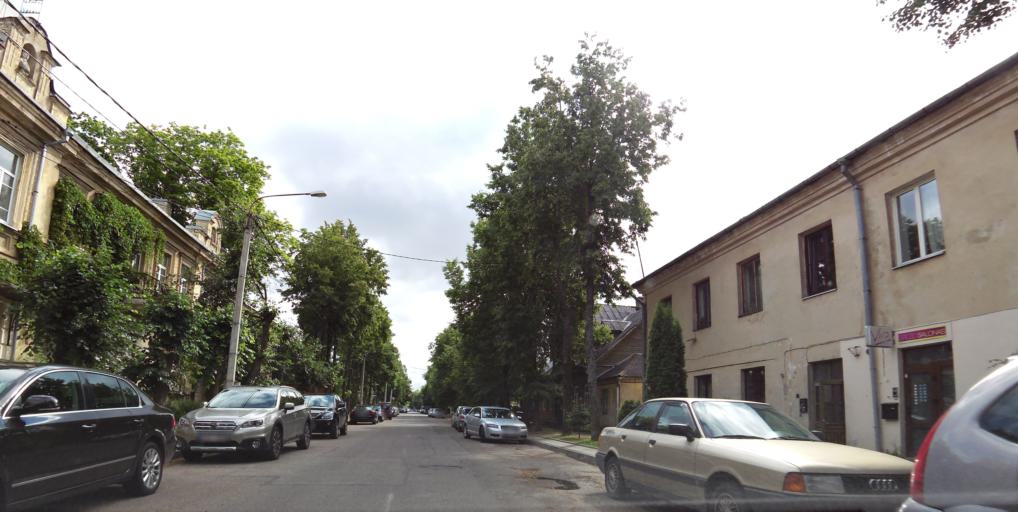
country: LT
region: Vilnius County
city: Seskine
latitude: 54.6915
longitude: 25.2496
